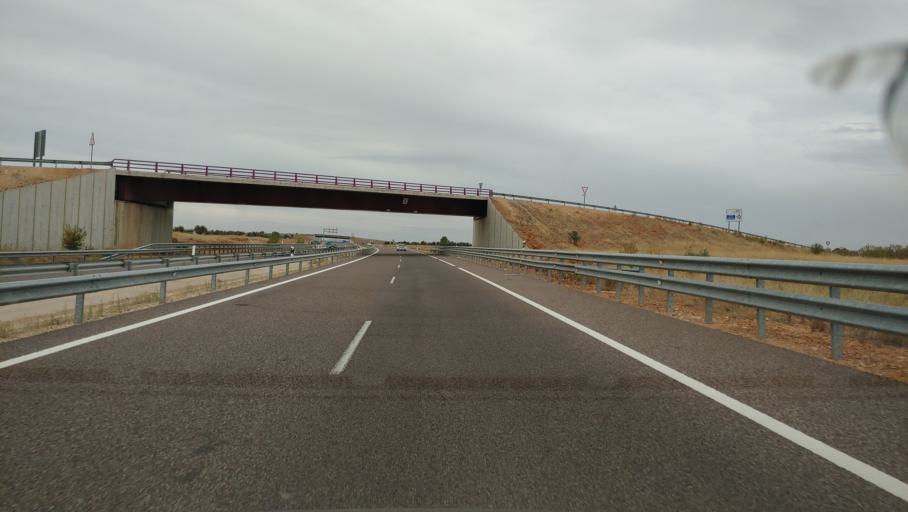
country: ES
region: Castille-La Mancha
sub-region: Provincia de Ciudad Real
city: Valenzuela de Calatrava
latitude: 38.9017
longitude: -3.8137
